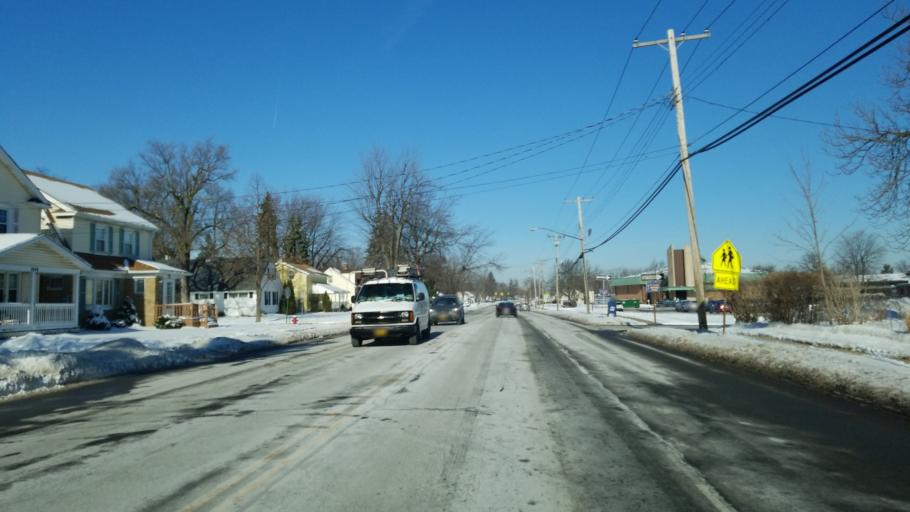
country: US
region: New York
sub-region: Erie County
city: Tonawanda
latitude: 42.9934
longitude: -78.8444
